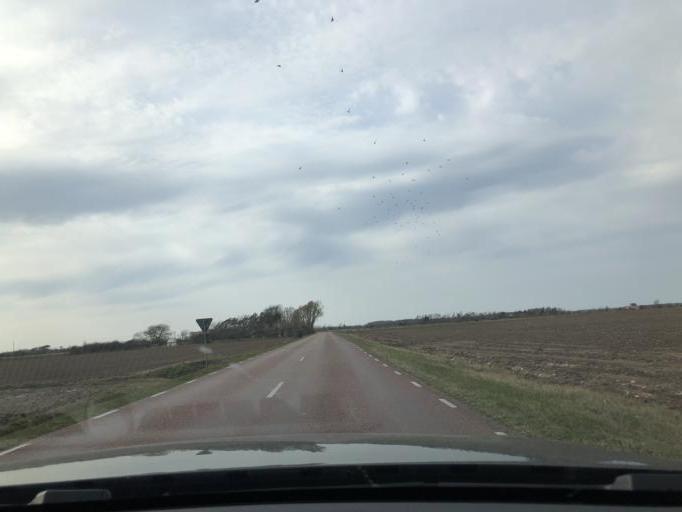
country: SE
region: Kalmar
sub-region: Morbylanga Kommun
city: Moerbylanga
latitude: 56.2850
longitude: 16.4932
